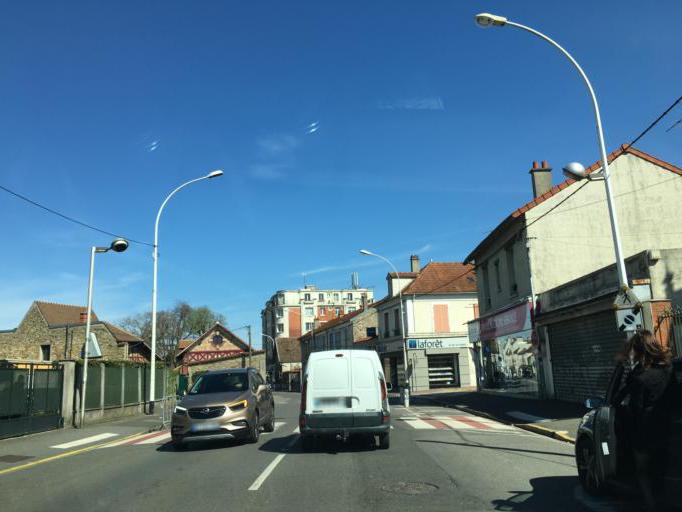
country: FR
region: Ile-de-France
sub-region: Departement de l'Essonne
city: Draveil
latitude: 48.6839
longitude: 2.4085
